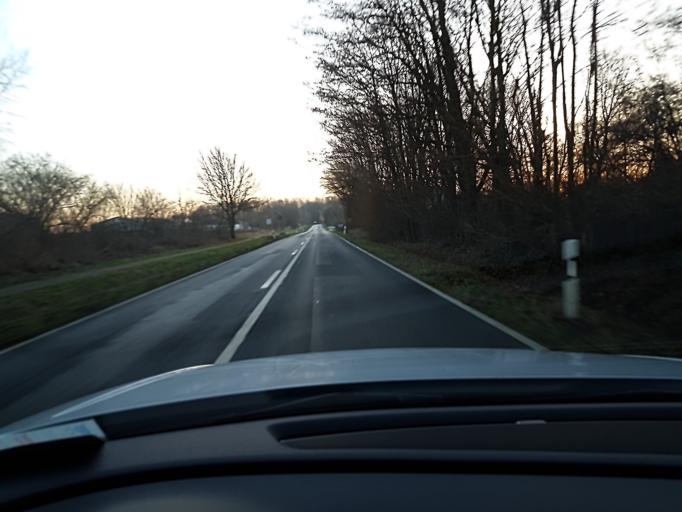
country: DE
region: Mecklenburg-Vorpommern
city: Wiek
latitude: 54.6127
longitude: 13.2835
